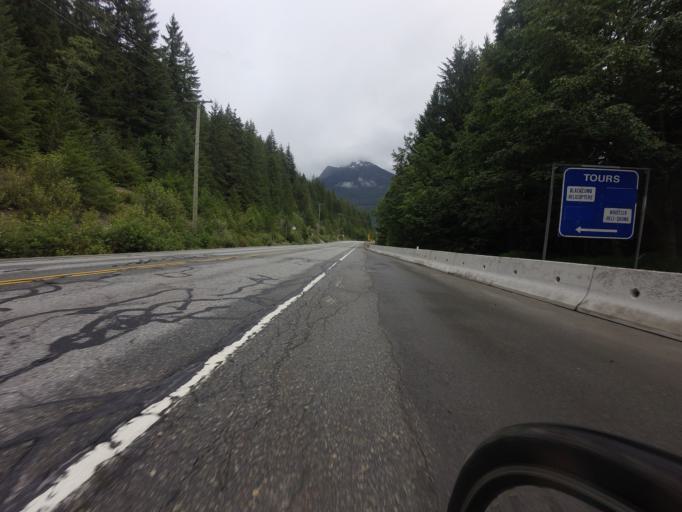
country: CA
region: British Columbia
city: Whistler
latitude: 50.1704
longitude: -122.9136
